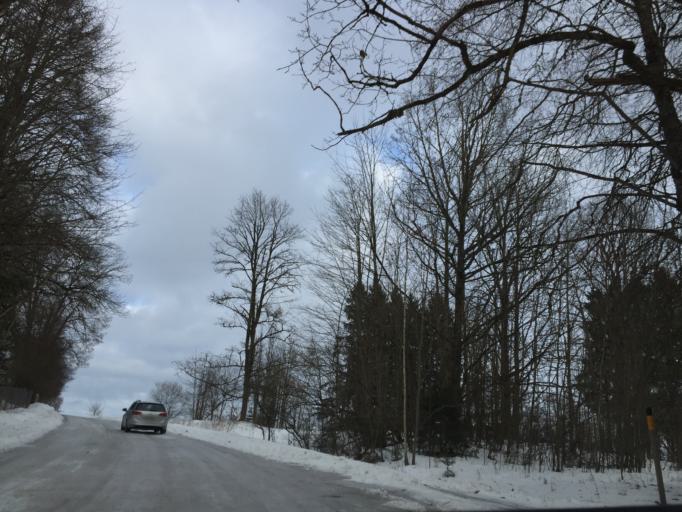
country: LV
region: Lielvarde
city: Lielvarde
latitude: 56.5766
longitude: 24.7372
